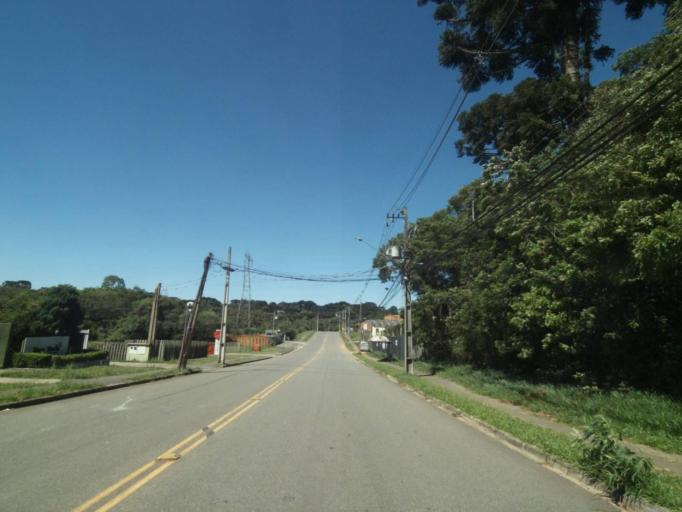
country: BR
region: Parana
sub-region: Curitiba
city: Curitiba
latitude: -25.4696
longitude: -49.3496
